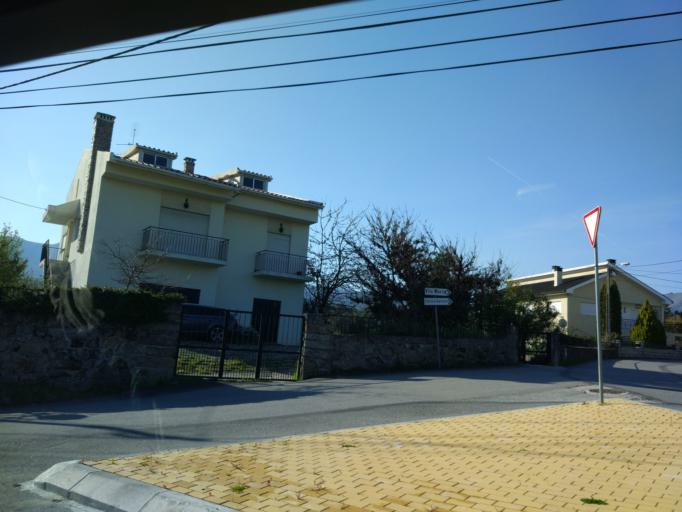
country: PT
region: Vila Real
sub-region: Vila Real
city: Vila Real
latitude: 41.2936
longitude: -7.7668
